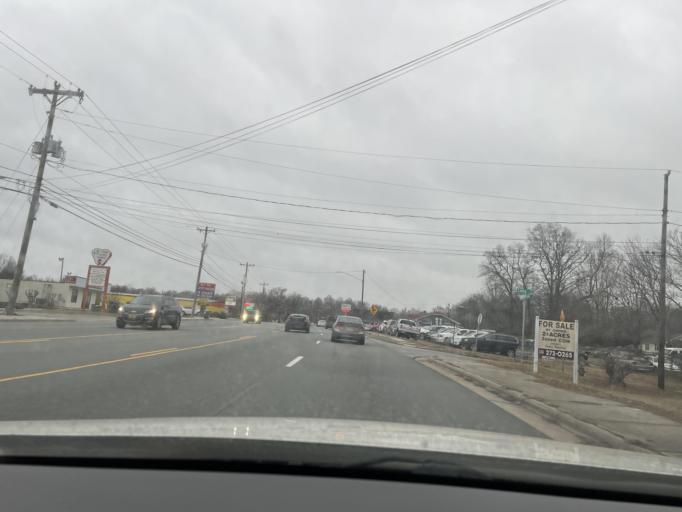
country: US
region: North Carolina
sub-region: Guilford County
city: Greensboro
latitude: 36.0260
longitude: -79.8026
